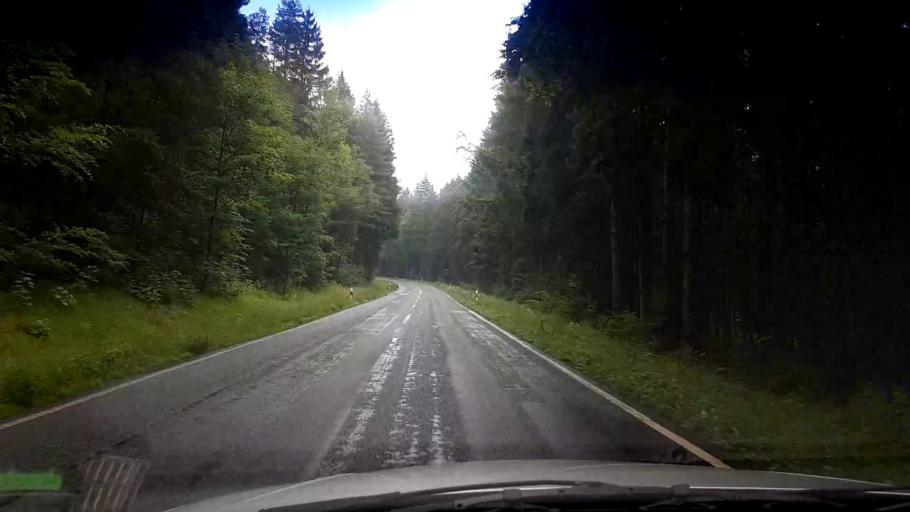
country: DE
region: Bavaria
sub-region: Upper Franconia
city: Weismain
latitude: 50.0865
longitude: 11.2704
